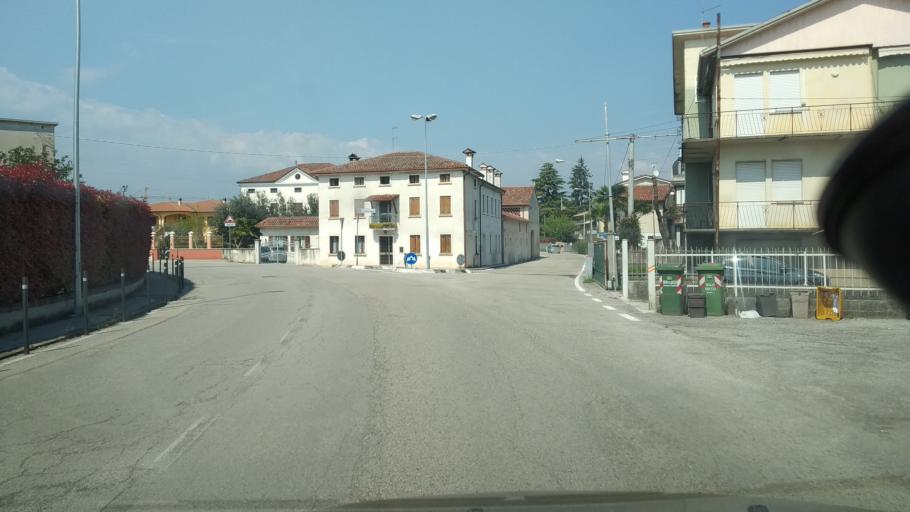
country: IT
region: Veneto
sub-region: Provincia di Vicenza
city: Dueville
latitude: 45.6294
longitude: 11.5749
